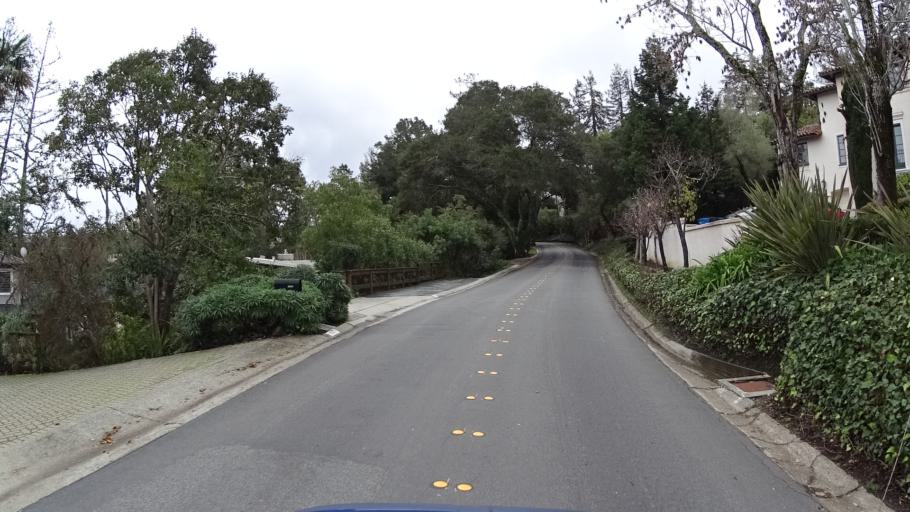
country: US
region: California
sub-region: San Mateo County
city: Burlingame
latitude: 37.5616
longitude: -122.3544
